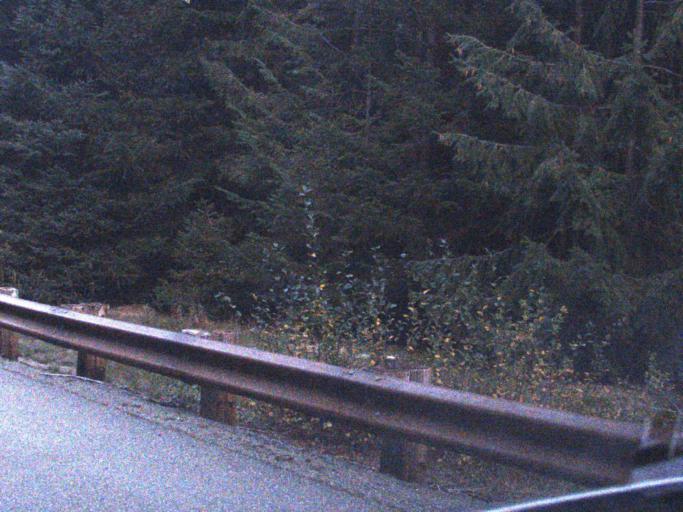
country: US
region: Washington
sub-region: Snohomish County
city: Darrington
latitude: 48.6476
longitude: -120.8572
